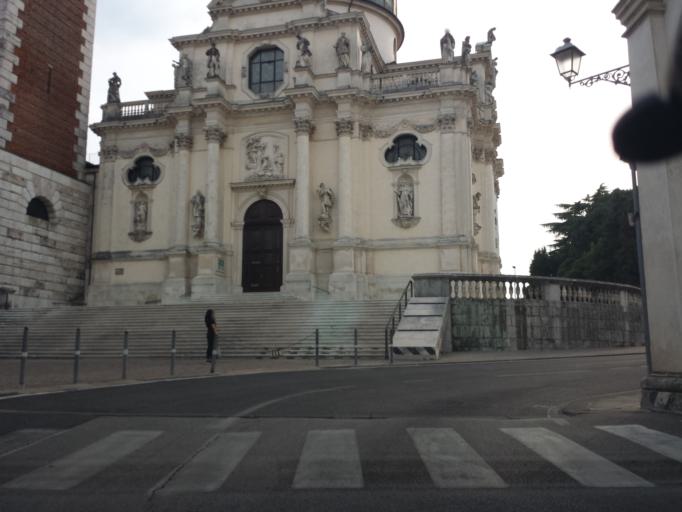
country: IT
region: Veneto
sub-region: Provincia di Vicenza
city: Vicenza
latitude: 45.5353
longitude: 11.5459
